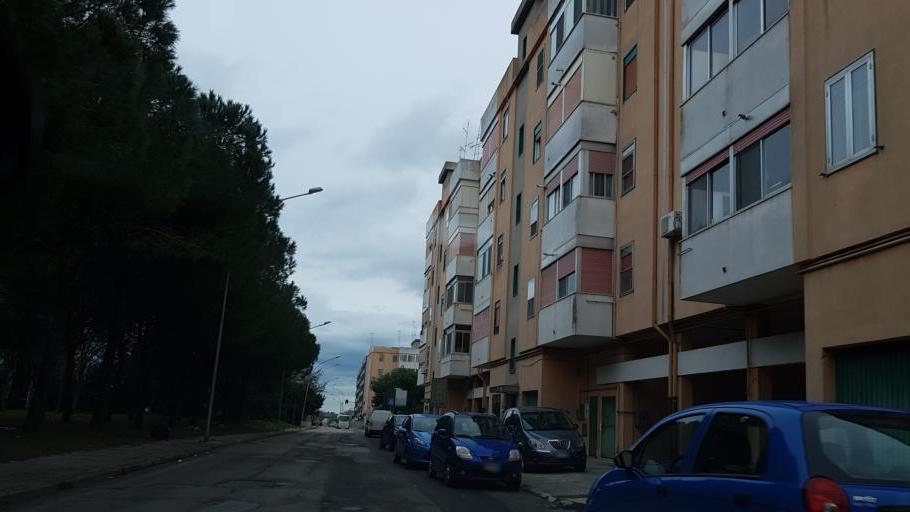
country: IT
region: Apulia
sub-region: Provincia di Brindisi
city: Brindisi
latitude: 40.6200
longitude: 17.9312
